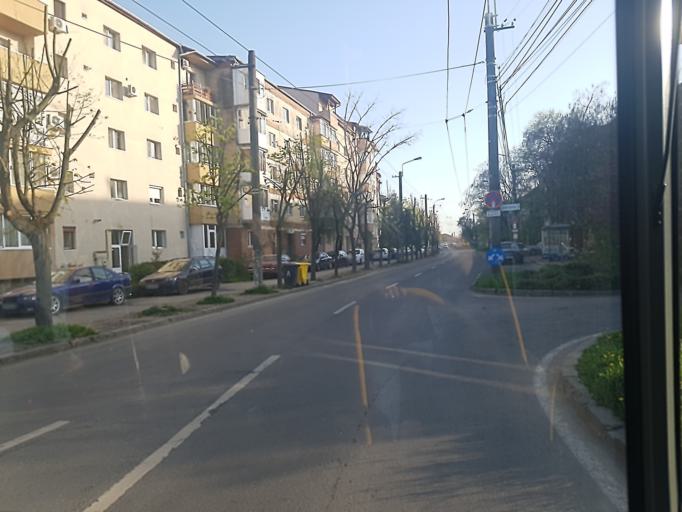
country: RO
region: Timis
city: Timisoara
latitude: 45.7364
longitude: 21.2501
